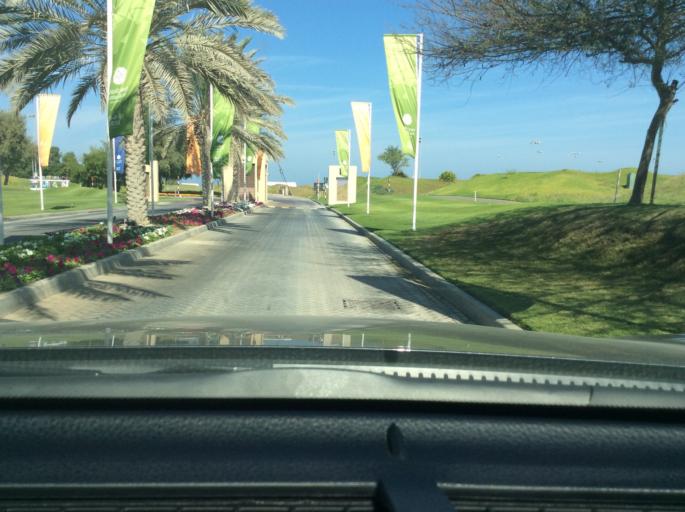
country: OM
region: Muhafazat Masqat
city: Bawshar
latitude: 23.6118
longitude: 58.3024
